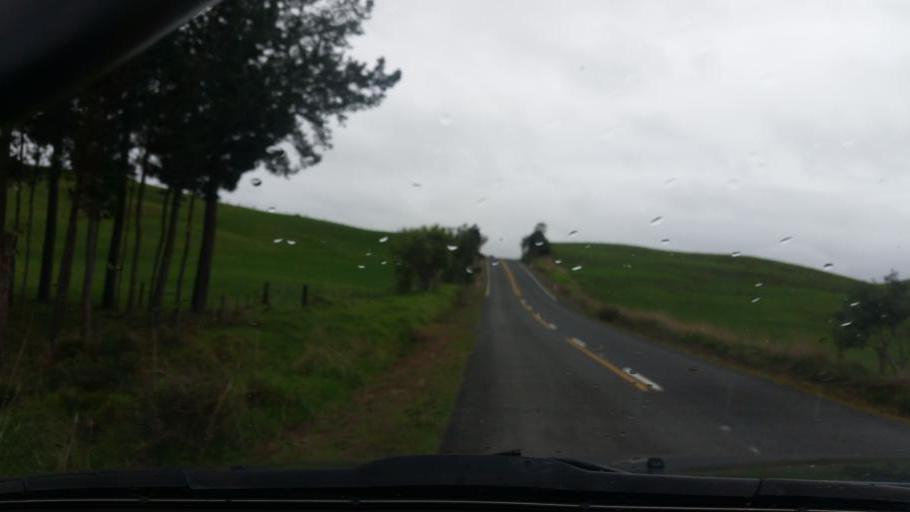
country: NZ
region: Northland
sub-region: Kaipara District
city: Dargaville
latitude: -36.0218
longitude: 173.9859
